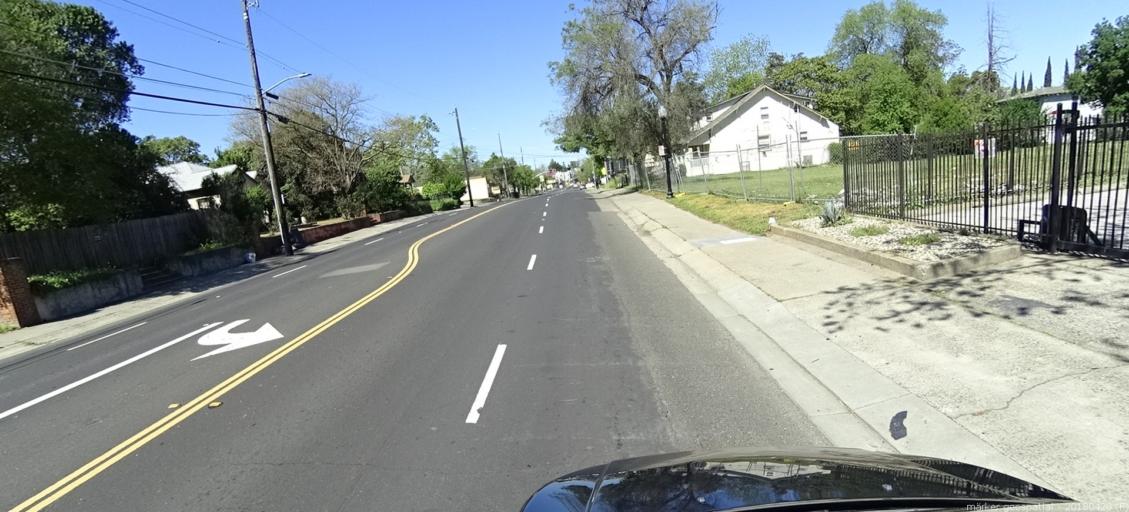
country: US
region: California
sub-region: Sacramento County
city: Sacramento
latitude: 38.5468
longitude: -121.4580
